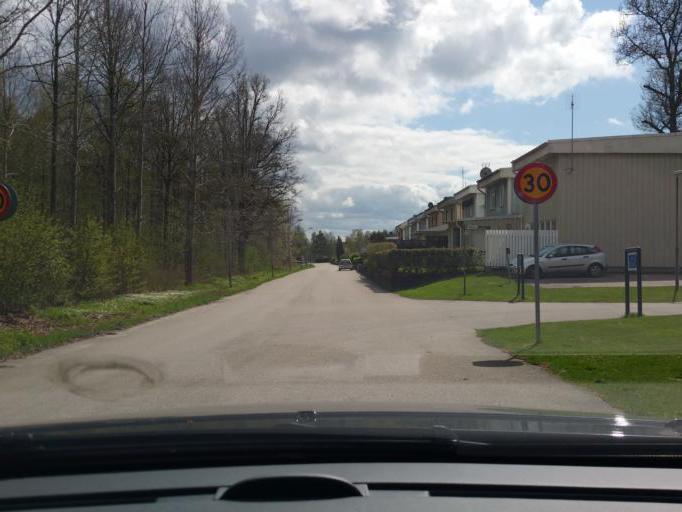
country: SE
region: Kronoberg
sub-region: Vaxjo Kommun
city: Lammhult
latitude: 57.1745
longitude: 14.5915
